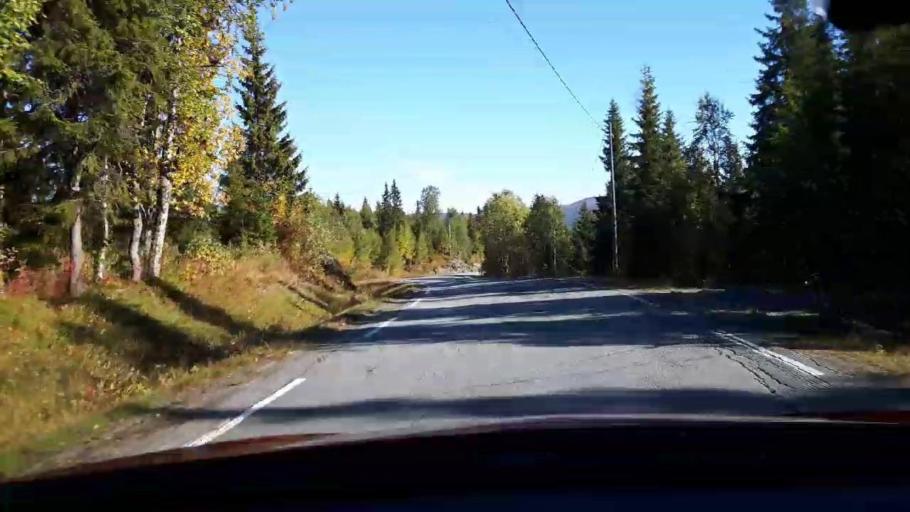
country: NO
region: Nord-Trondelag
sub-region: Lierne
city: Sandvika
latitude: 64.6271
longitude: 13.6863
